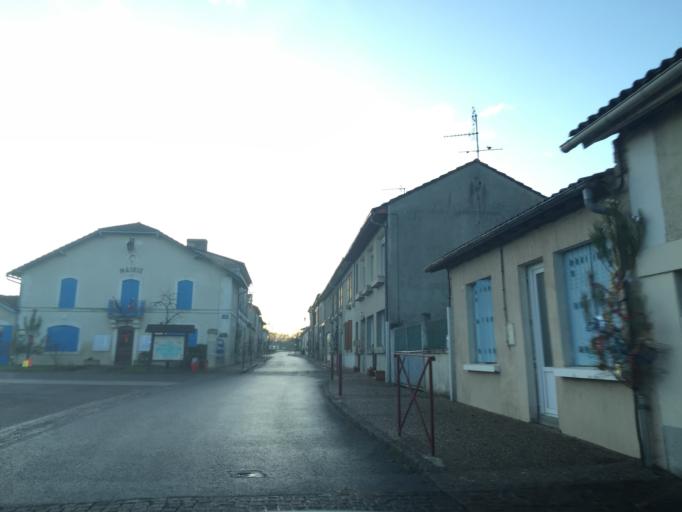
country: FR
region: Aquitaine
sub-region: Departement de la Dordogne
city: Saint-Aulaye
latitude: 45.2564
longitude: 0.1988
